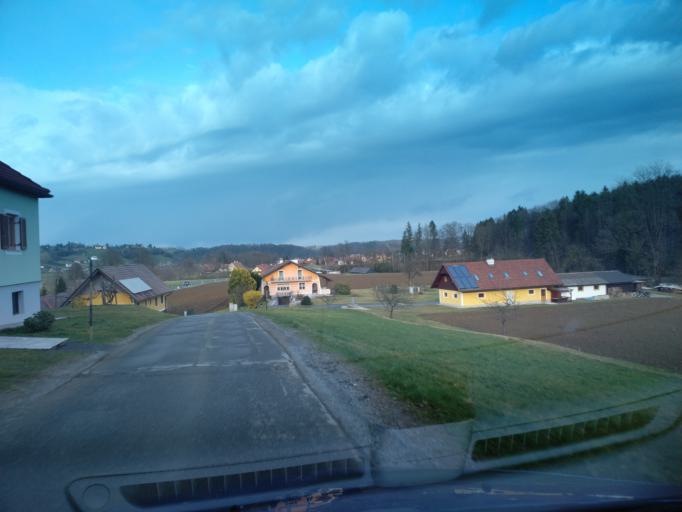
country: AT
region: Styria
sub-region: Politischer Bezirk Deutschlandsberg
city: Pitschgau
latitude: 46.6940
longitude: 15.2714
